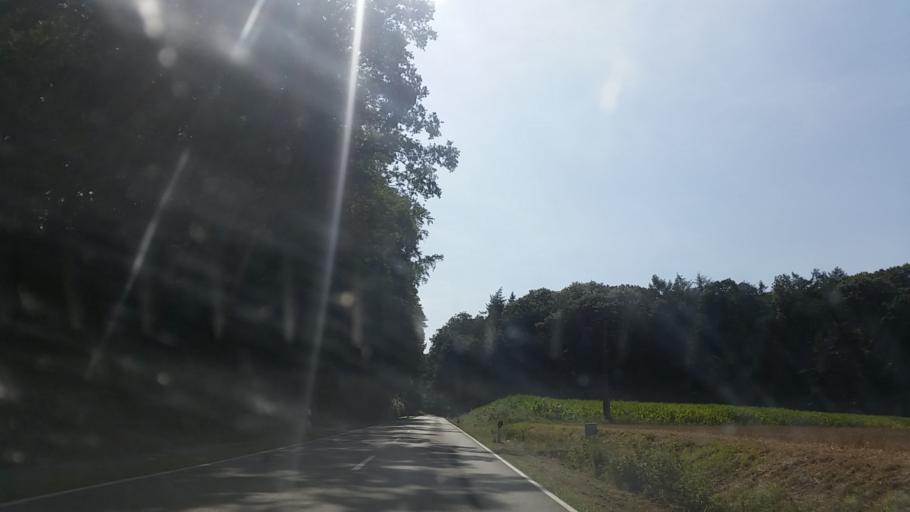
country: DE
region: Lower Saxony
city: Ankum
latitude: 52.5239
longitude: 7.8980
